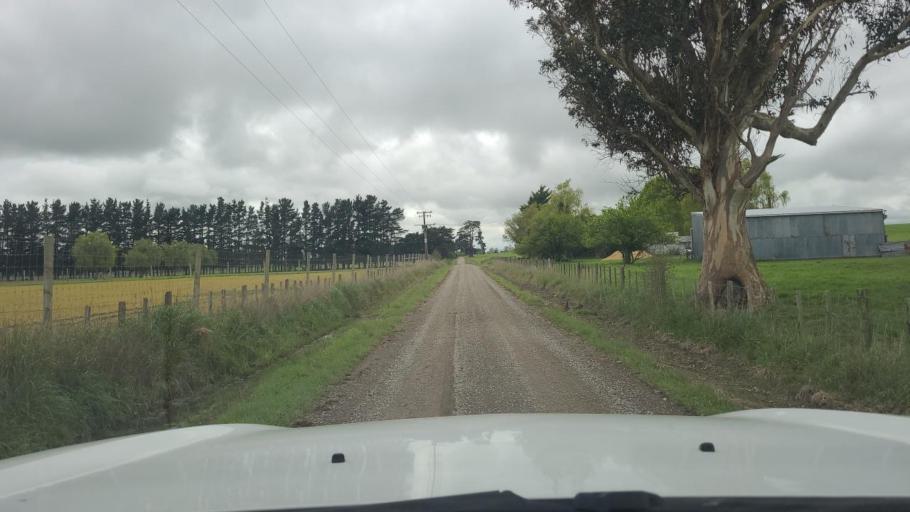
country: NZ
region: Wellington
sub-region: Masterton District
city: Masterton
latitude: -41.0521
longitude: 175.5210
